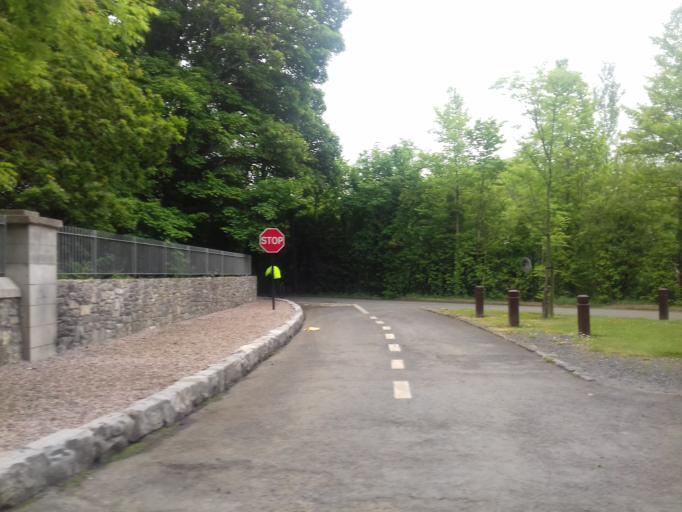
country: IE
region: Leinster
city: Donabate
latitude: 53.4879
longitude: -6.1784
